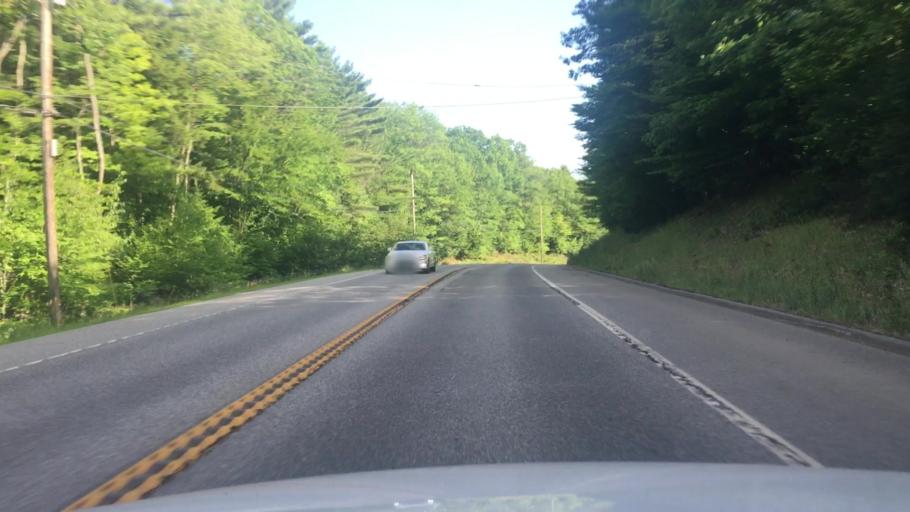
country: US
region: Maine
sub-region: Androscoggin County
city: Livermore
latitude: 44.4167
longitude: -70.2200
